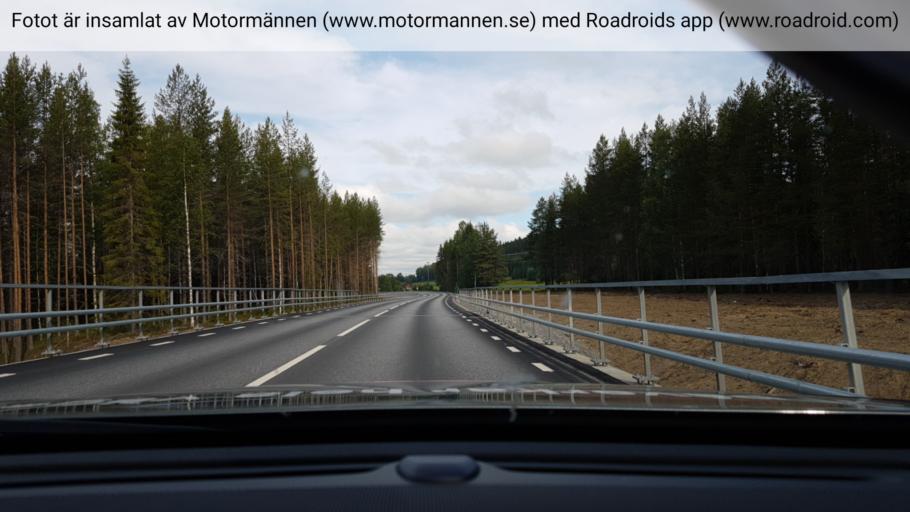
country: SE
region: Vaesterbotten
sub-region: Vindelns Kommun
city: Vindeln
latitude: 64.1757
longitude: 19.7359
